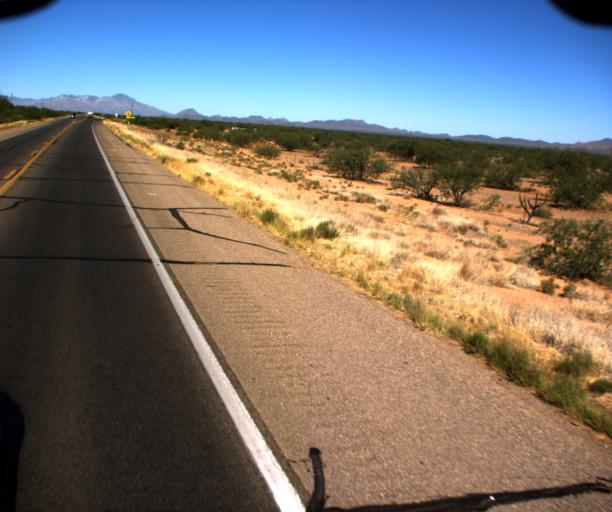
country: US
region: Arizona
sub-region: Pima County
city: Valencia West
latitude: 32.1168
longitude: -111.2132
